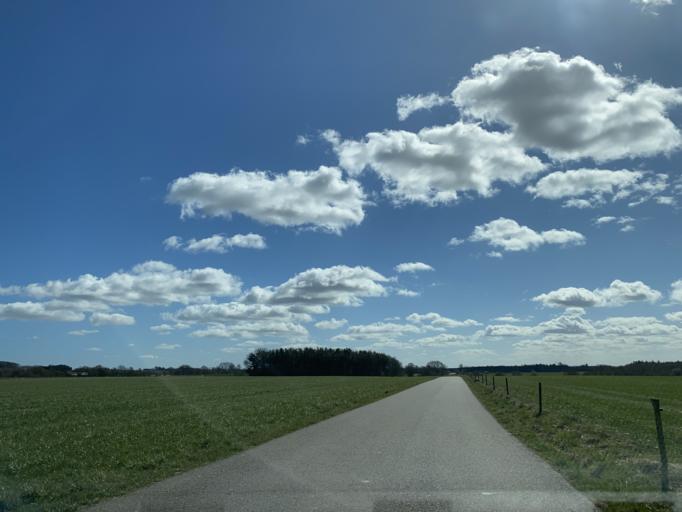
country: DK
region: Central Jutland
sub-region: Favrskov Kommune
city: Ulstrup
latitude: 56.3277
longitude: 9.7900
